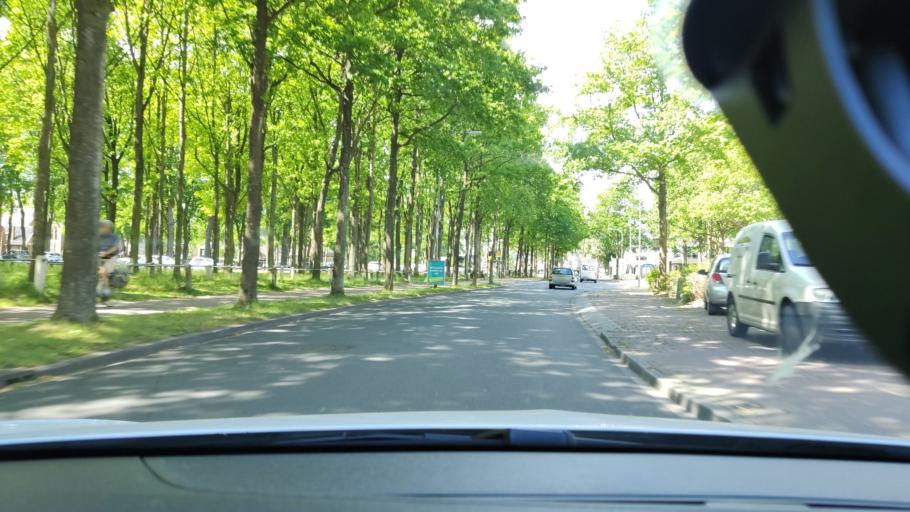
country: NL
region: Drenthe
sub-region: Gemeente Tynaarlo
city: Zuidlaren
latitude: 53.0926
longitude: 6.6887
